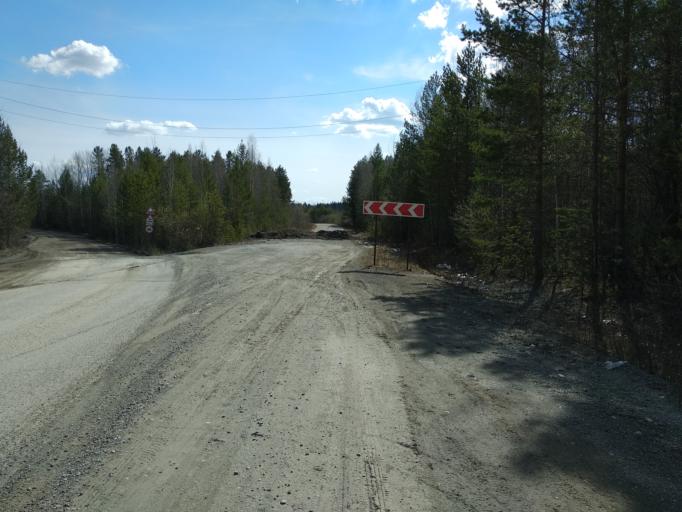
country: RU
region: Sverdlovsk
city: Rudnichnyy
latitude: 59.6827
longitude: 60.2086
